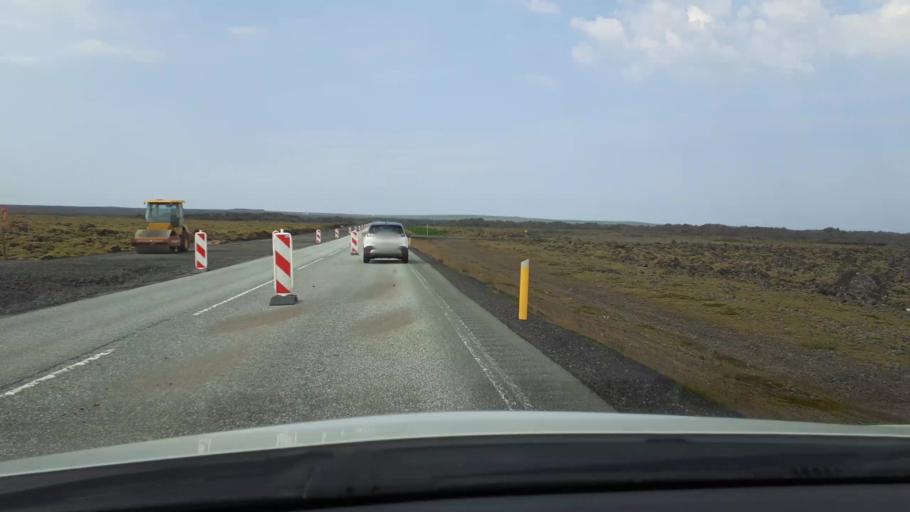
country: IS
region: Southern Peninsula
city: Vogar
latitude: 63.9217
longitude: -22.4219
